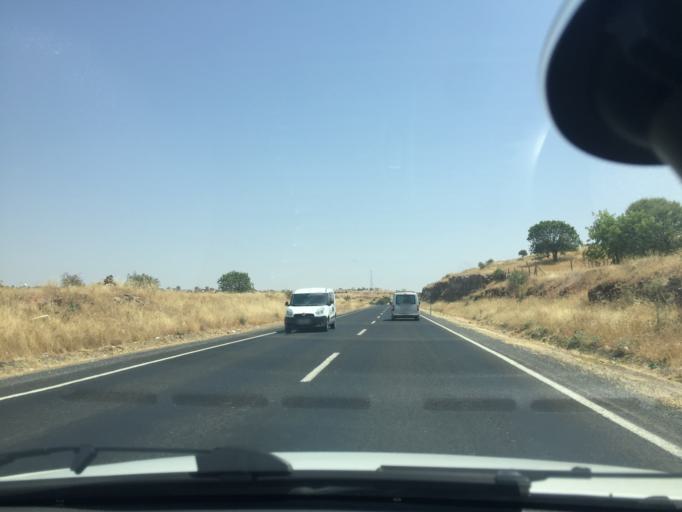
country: TR
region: Mardin
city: Acirli
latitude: 37.4499
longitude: 41.2672
